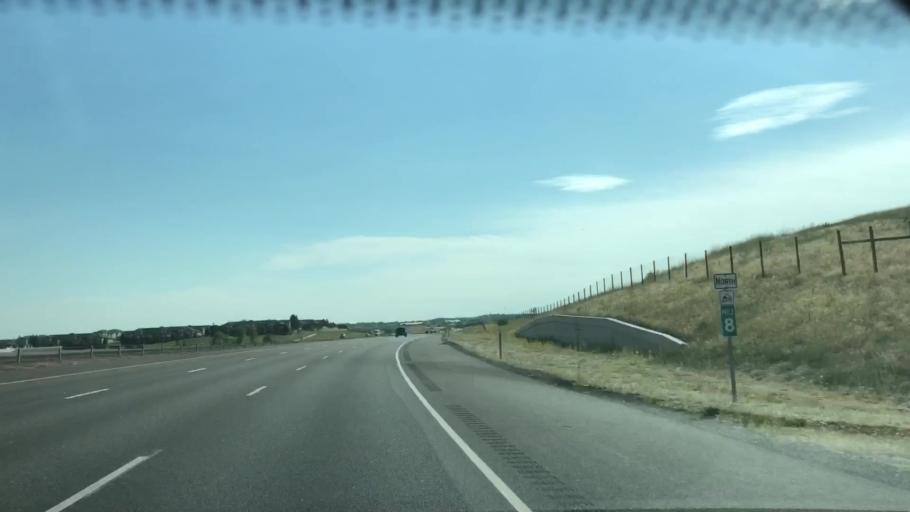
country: US
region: Colorado
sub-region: Douglas County
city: Parker
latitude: 39.5765
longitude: -104.7421
